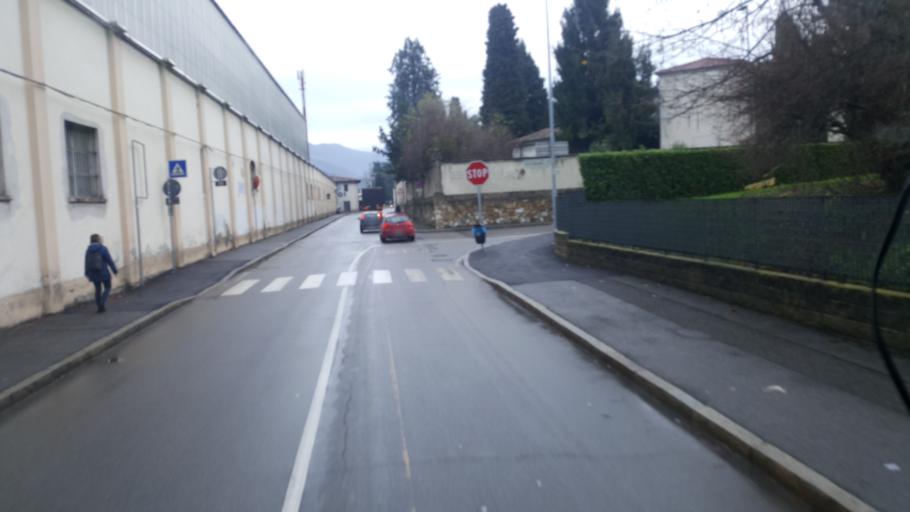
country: IT
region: Lombardy
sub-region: Provincia di Bergamo
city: Bergamo
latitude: 45.6986
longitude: 9.6875
